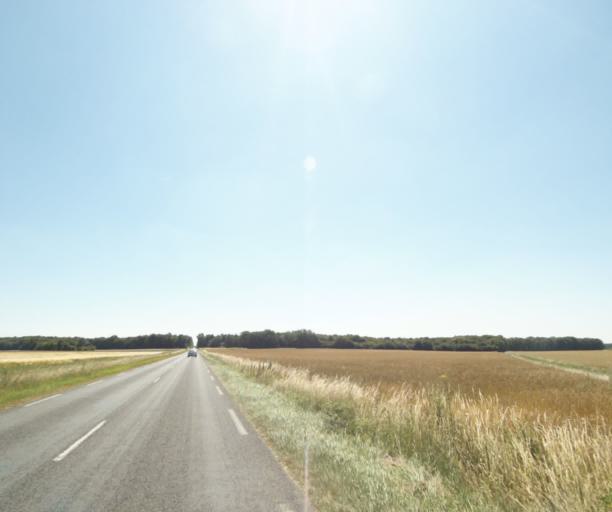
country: FR
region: Centre
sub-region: Departement du Loiret
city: Malesherbes
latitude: 48.3204
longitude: 2.4434
